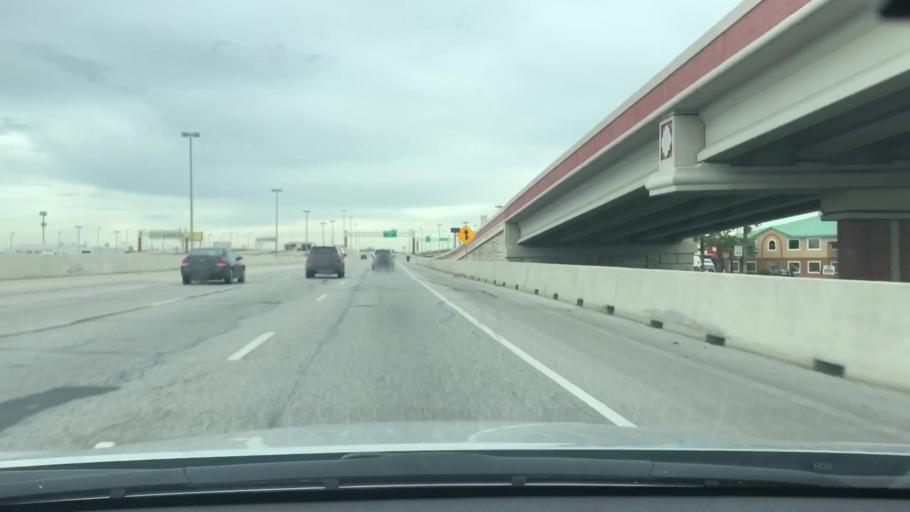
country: US
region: Texas
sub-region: Bexar County
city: Alamo Heights
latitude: 29.5191
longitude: -98.4736
